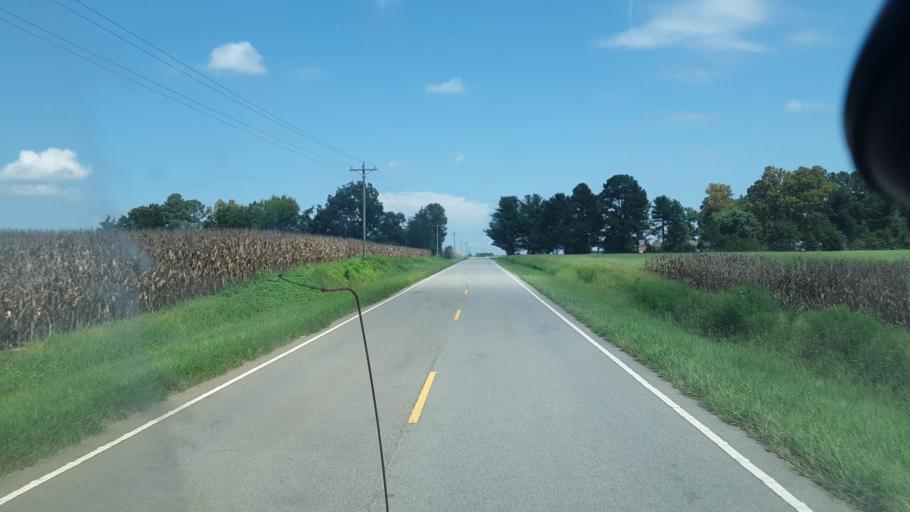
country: US
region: South Carolina
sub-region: Orangeburg County
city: Edisto
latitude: 33.4260
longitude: -81.0182
